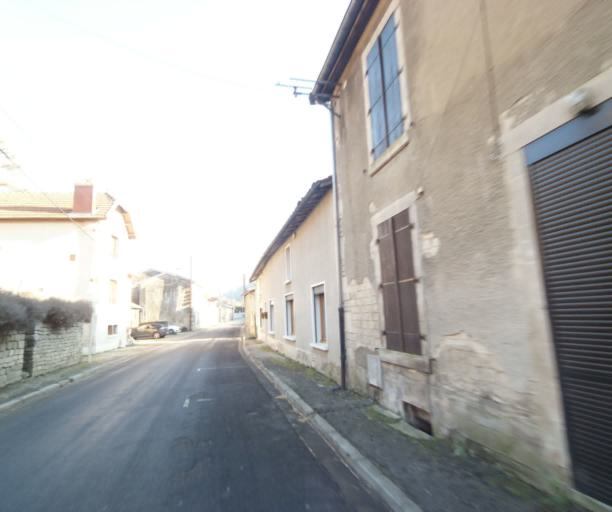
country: FR
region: Champagne-Ardenne
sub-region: Departement de la Haute-Marne
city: Chevillon
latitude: 48.5280
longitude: 5.1418
